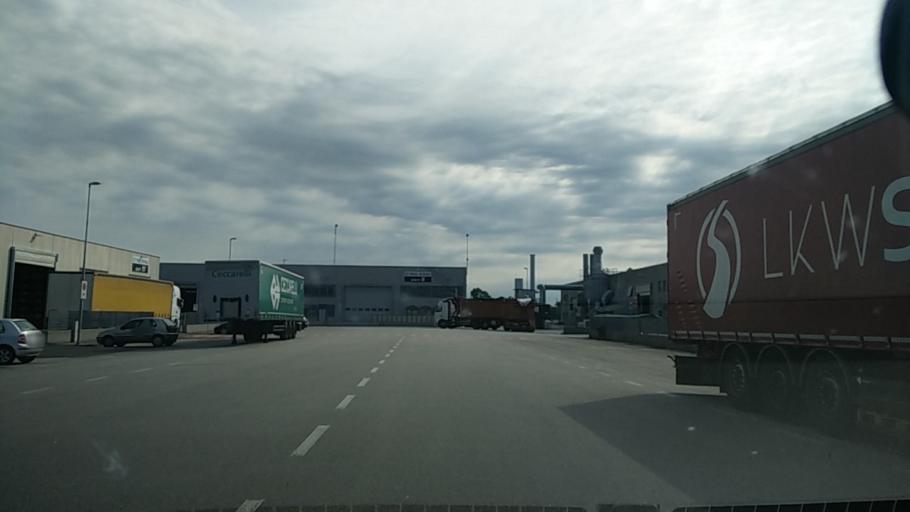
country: IT
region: Veneto
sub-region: Provincia di Treviso
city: Portobuffole
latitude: 45.8528
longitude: 12.5074
